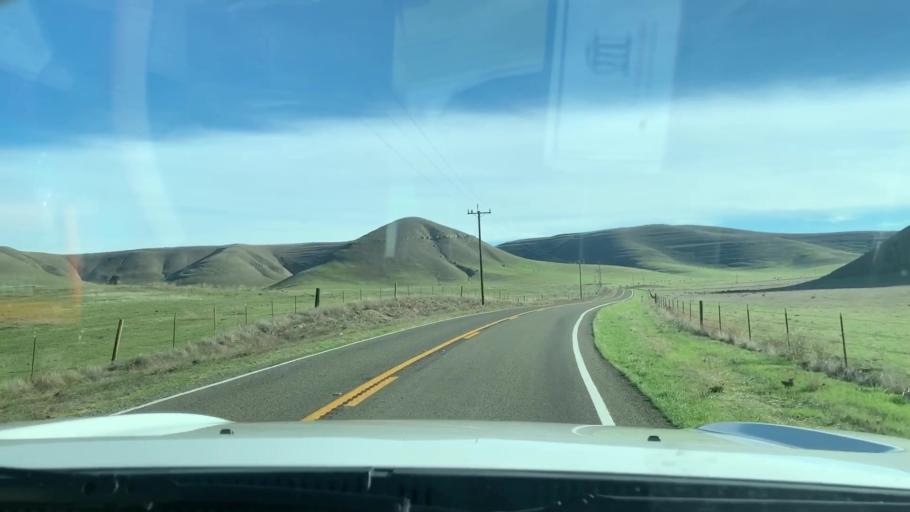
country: US
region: California
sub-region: Monterey County
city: King City
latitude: 36.1577
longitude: -120.9895
